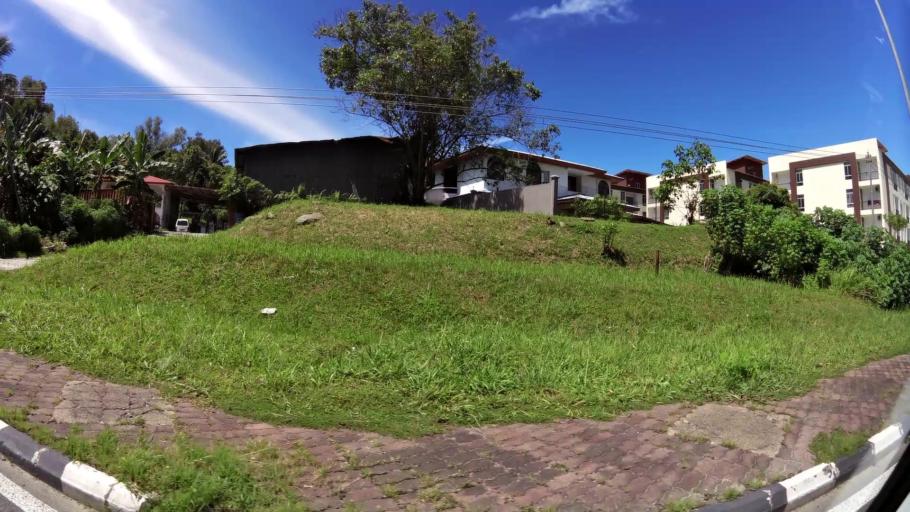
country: BN
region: Brunei and Muara
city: Bandar Seri Begawan
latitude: 5.0309
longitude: 115.0559
